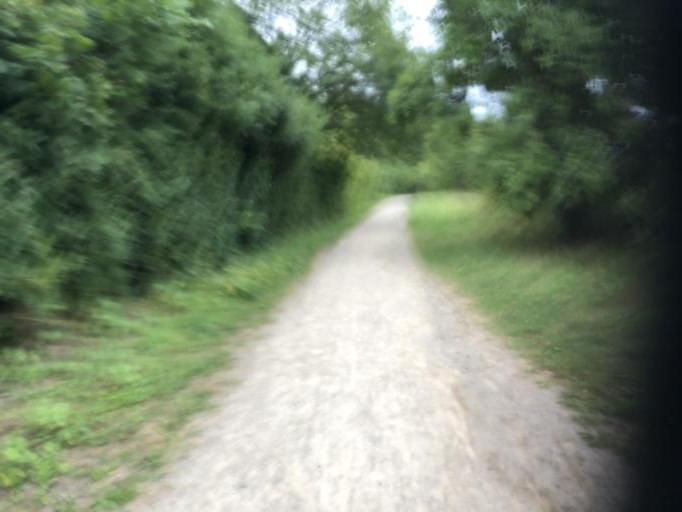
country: DE
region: North Rhine-Westphalia
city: Witten
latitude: 51.4903
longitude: 7.3984
